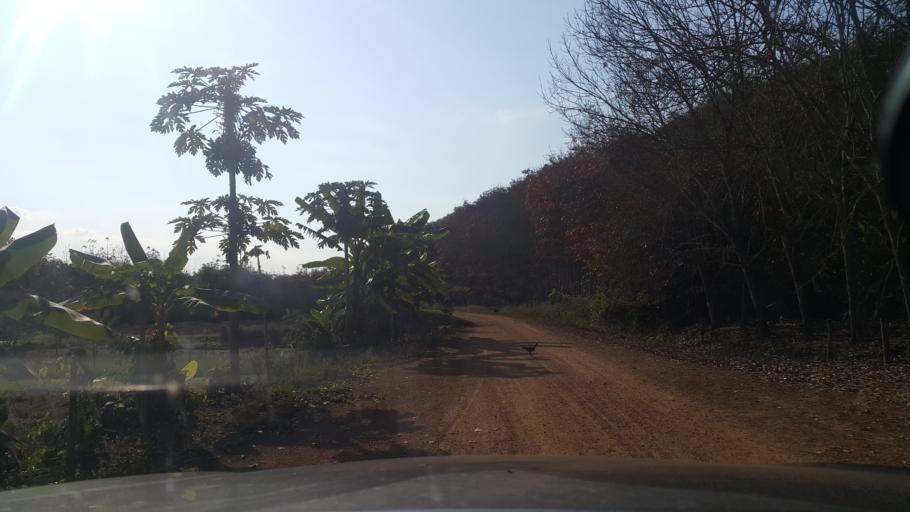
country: TH
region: Loei
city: Chiang Khan
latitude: 17.8341
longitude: 101.6082
